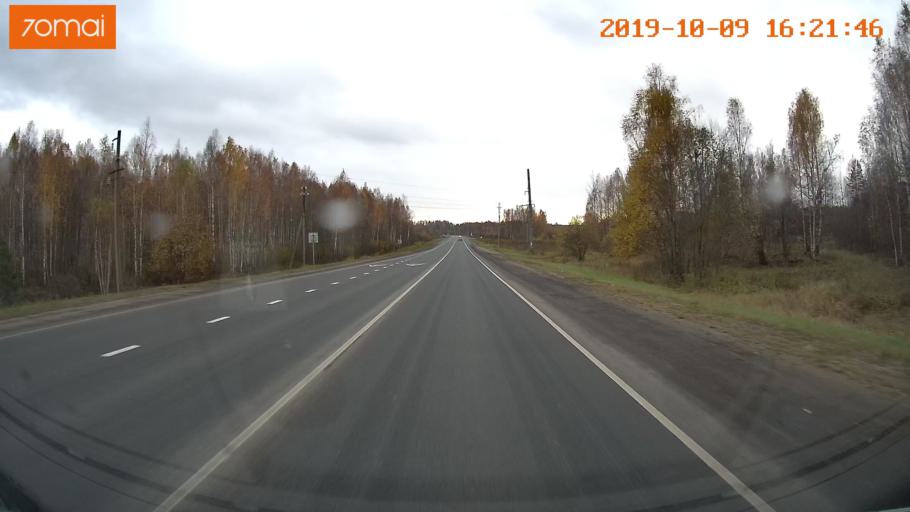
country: RU
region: Kostroma
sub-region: Kostromskoy Rayon
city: Kostroma
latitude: 57.6869
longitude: 40.8881
